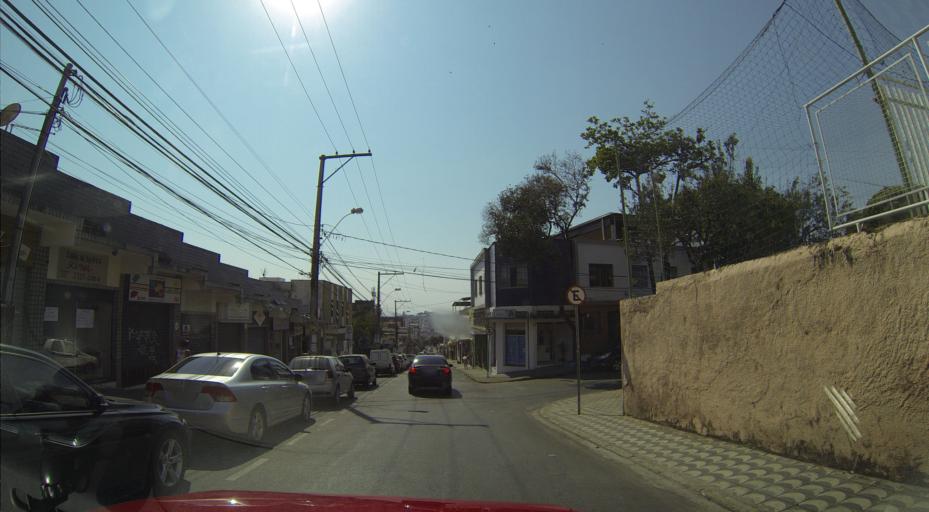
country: BR
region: Minas Gerais
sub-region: Belo Horizonte
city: Belo Horizonte
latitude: -19.9064
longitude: -43.9707
